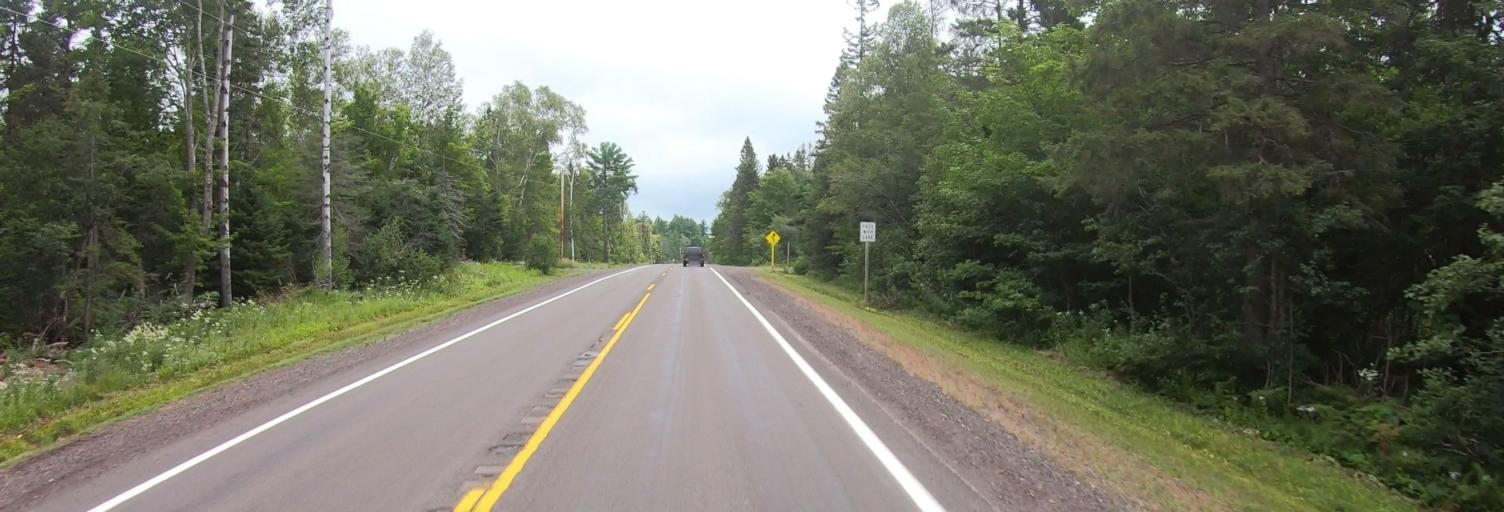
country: US
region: Michigan
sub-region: Keweenaw County
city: Eagle River
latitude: 47.4066
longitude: -88.1854
